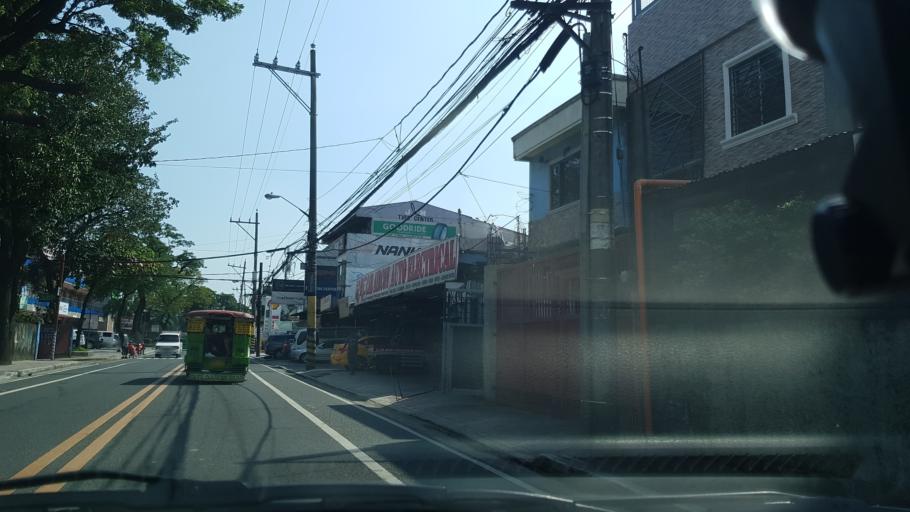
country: PH
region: Metro Manila
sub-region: Marikina
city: Calumpang
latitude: 14.6470
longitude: 121.0968
